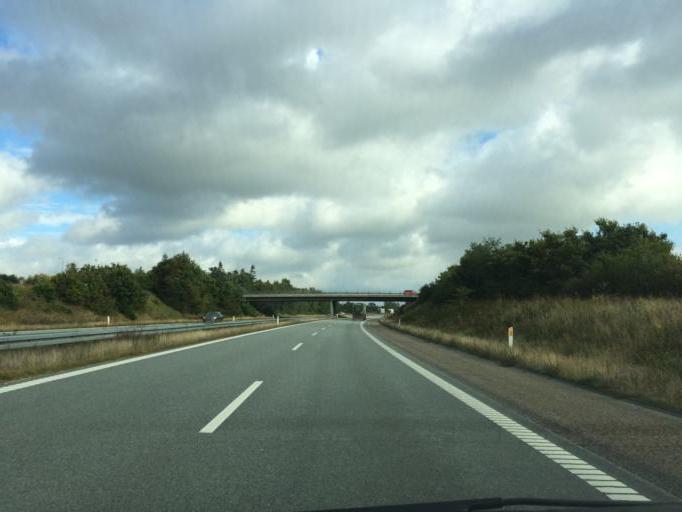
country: DK
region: North Denmark
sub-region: Alborg Kommune
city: Vodskov
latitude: 57.1126
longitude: 10.0553
